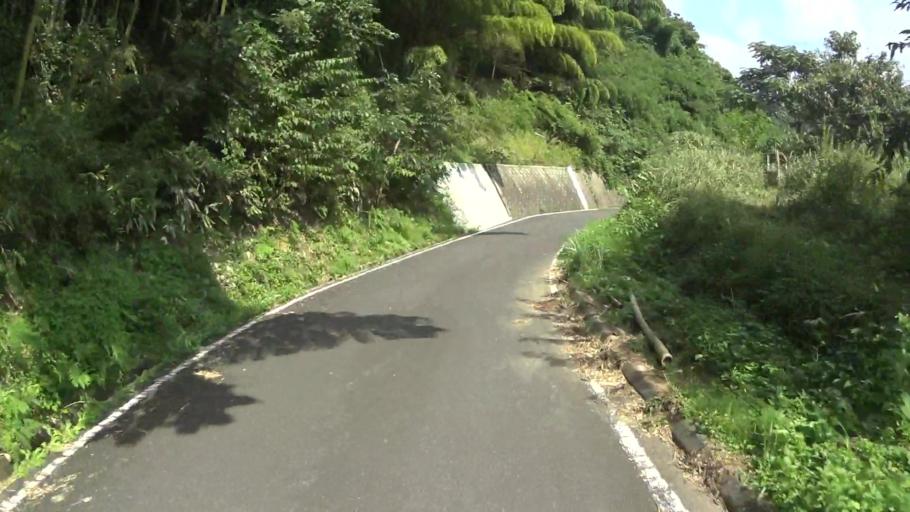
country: JP
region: Kyoto
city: Miyazu
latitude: 35.6677
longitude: 135.2354
